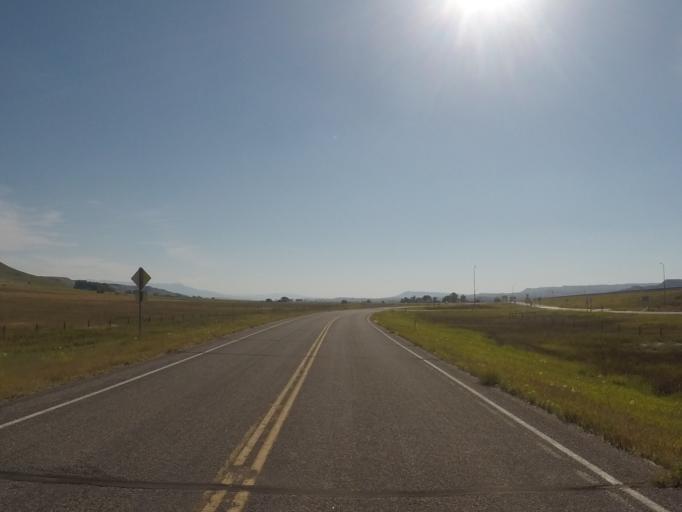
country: US
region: Montana
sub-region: Sweet Grass County
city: Big Timber
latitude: 45.8245
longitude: -109.9706
